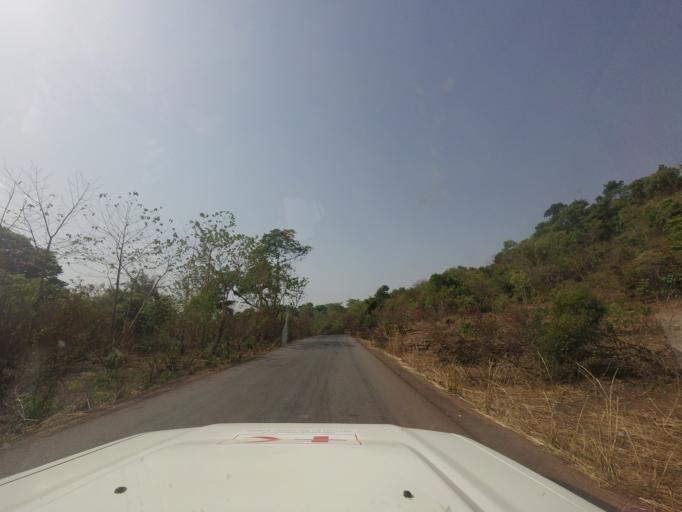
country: GN
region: Mamou
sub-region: Mamou Prefecture
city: Mamou
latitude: 10.2010
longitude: -12.4669
